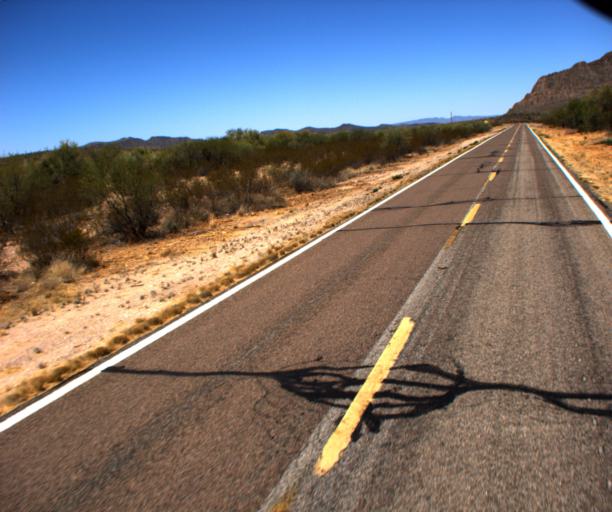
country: US
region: Arizona
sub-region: Pima County
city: Ajo
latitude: 32.2226
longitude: -112.6726
